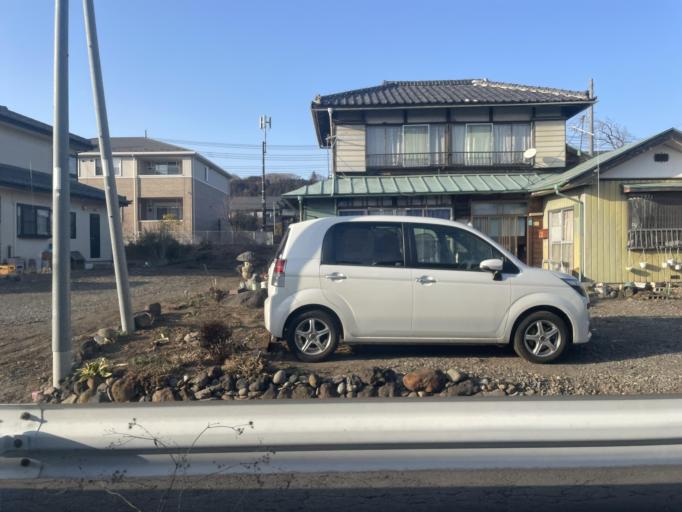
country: JP
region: Gunma
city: Nakanojomachi
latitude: 36.5855
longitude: 138.8578
